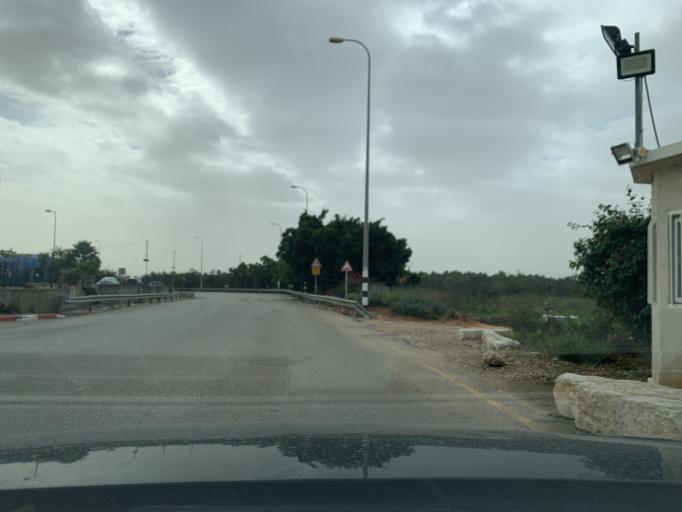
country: IL
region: Central District
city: Jaljulya
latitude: 32.1558
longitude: 34.9466
